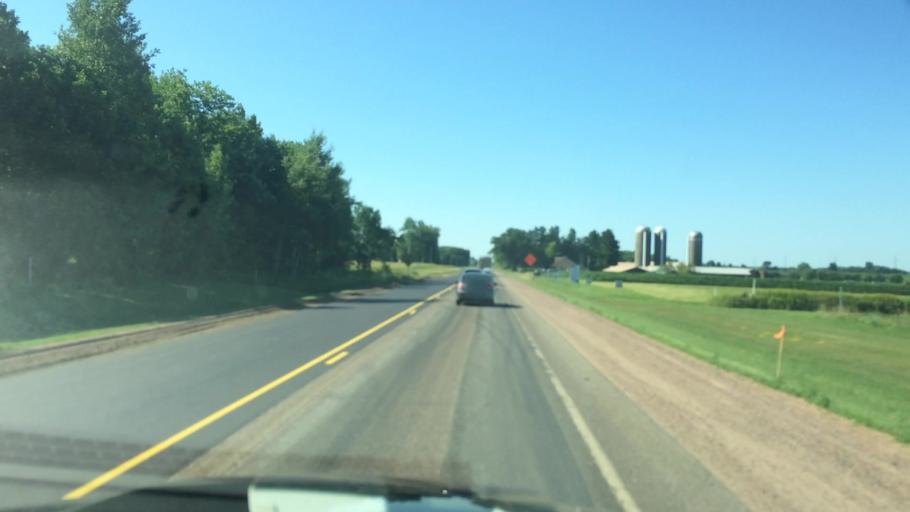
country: US
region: Wisconsin
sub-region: Marathon County
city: Stratford
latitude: 44.8665
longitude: -90.0791
